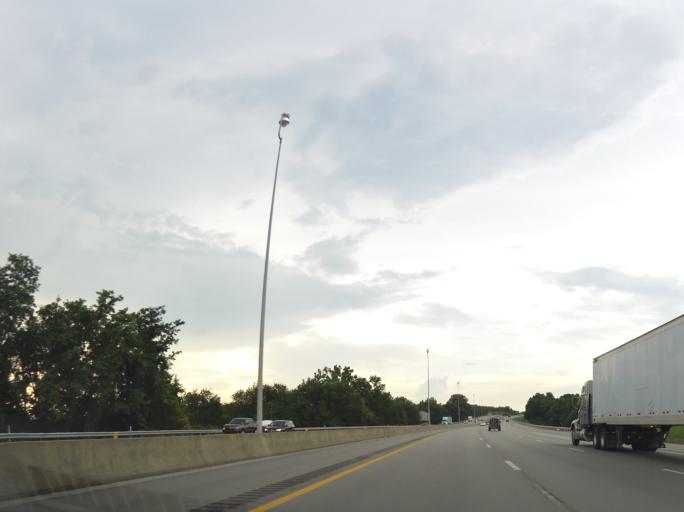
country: US
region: Kentucky
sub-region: Fayette County
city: Lexington
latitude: 37.8945
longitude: -84.3530
